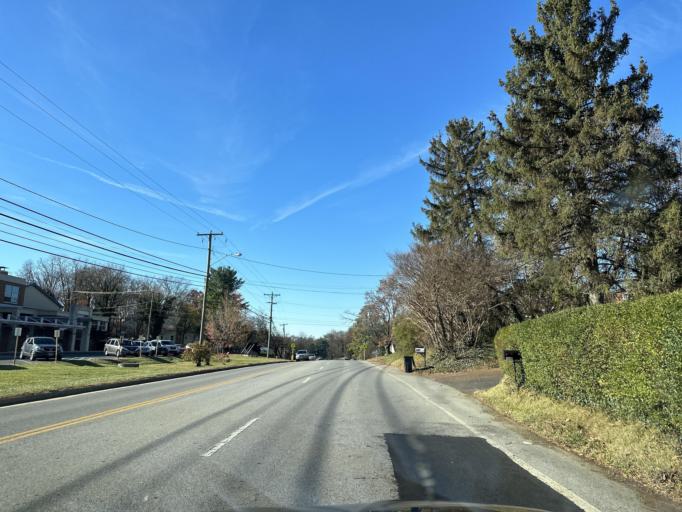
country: US
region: Virginia
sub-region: City of Staunton
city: Staunton
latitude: 38.1643
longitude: -79.0572
